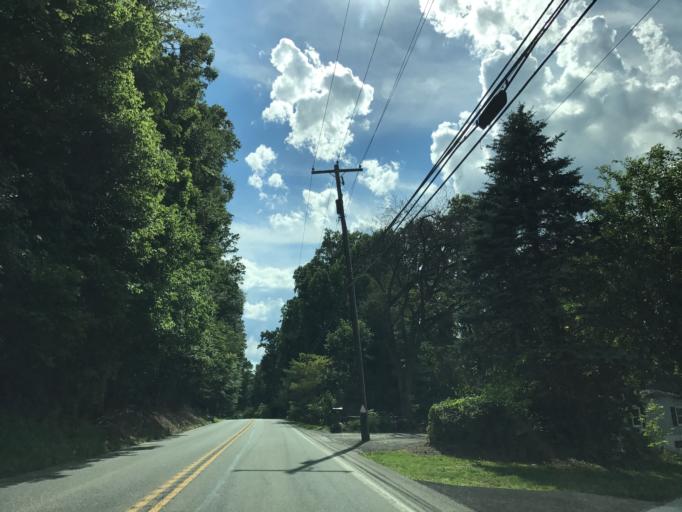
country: US
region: Pennsylvania
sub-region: Lancaster County
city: Conestoga
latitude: 39.9076
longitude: -76.3186
